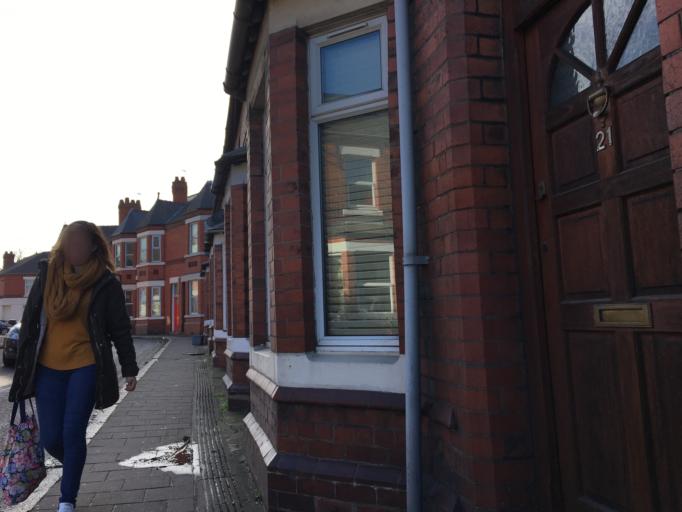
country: GB
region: England
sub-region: Cheshire West and Chester
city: Hoole
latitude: 53.1995
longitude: -2.8820
